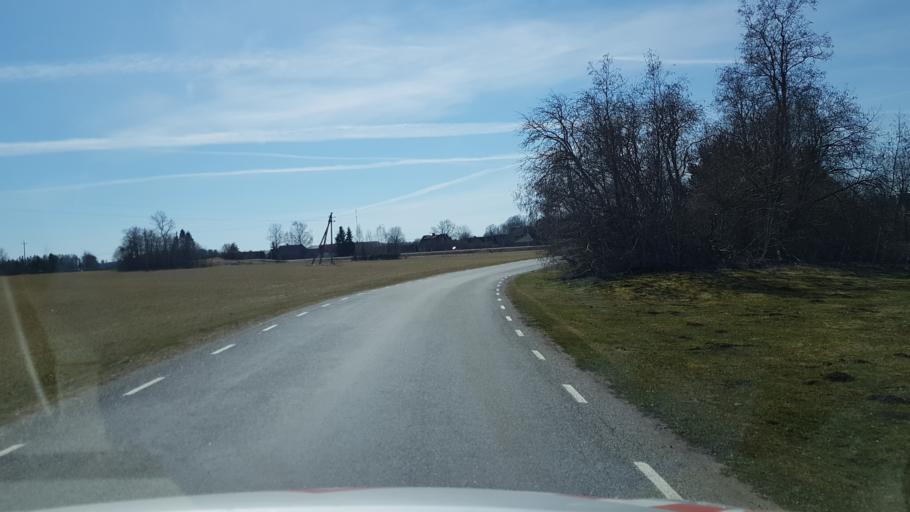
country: EE
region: Laeaene-Virumaa
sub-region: Vinni vald
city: Vinni
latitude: 59.2827
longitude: 26.4244
